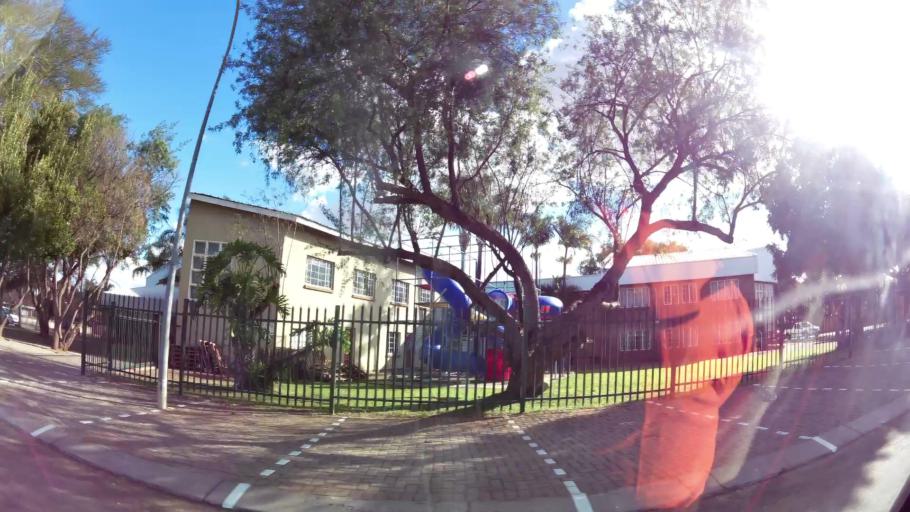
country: ZA
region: Limpopo
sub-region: Capricorn District Municipality
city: Polokwane
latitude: -23.9045
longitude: 29.4955
